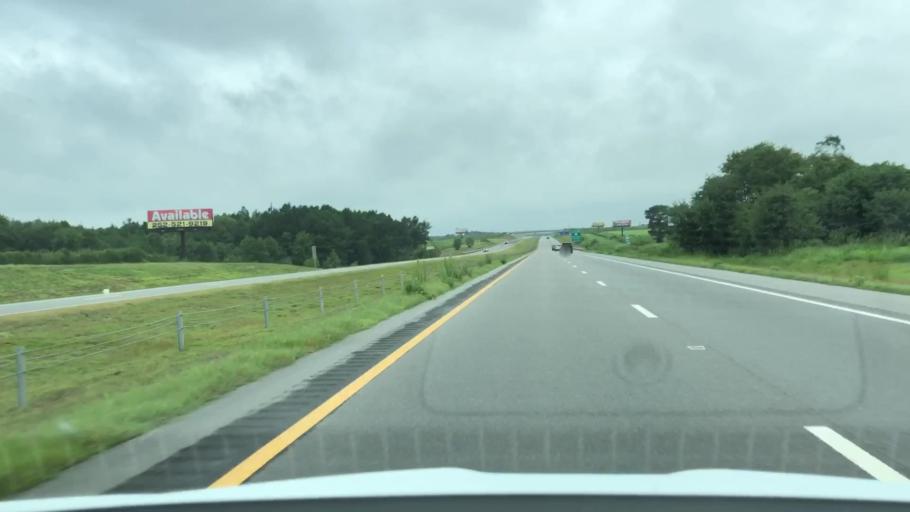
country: US
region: North Carolina
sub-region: Wayne County
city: Elroy
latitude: 35.4048
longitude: -77.8803
